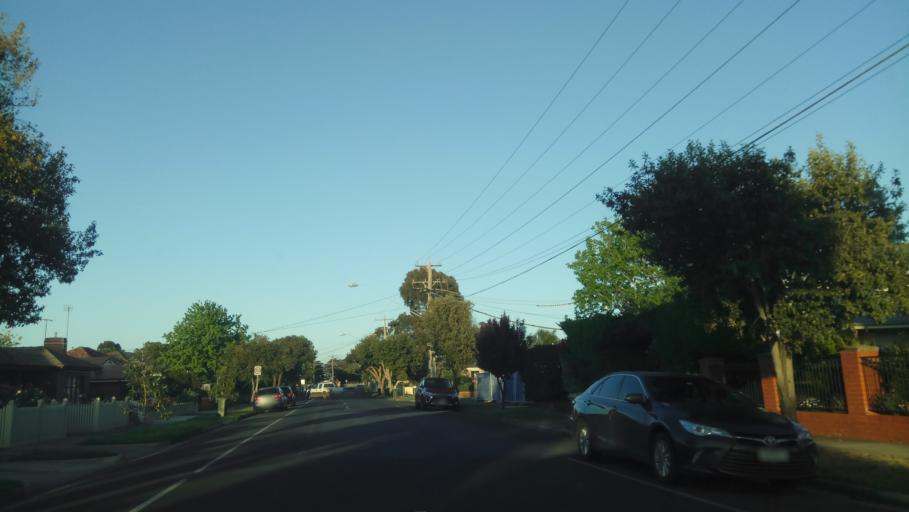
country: AU
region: Victoria
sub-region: Hobsons Bay
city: Altona
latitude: -37.8701
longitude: 144.8139
